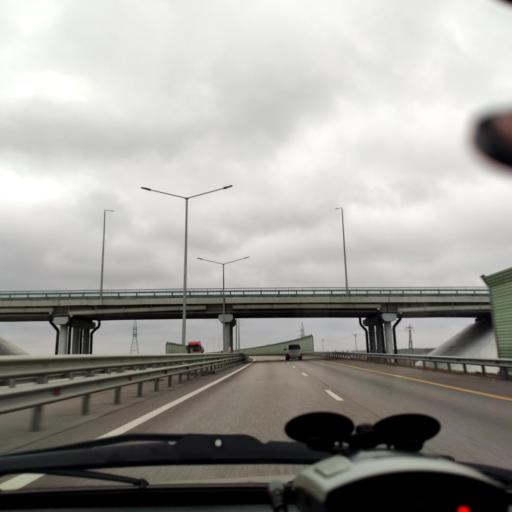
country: RU
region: Voronezj
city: Novaya Usman'
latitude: 51.6147
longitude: 39.3191
